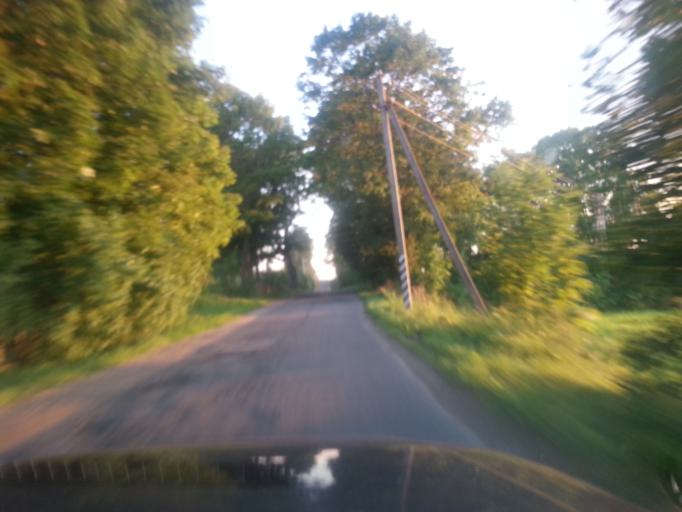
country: BY
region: Minsk
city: Narach
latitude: 54.9721
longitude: 26.6389
